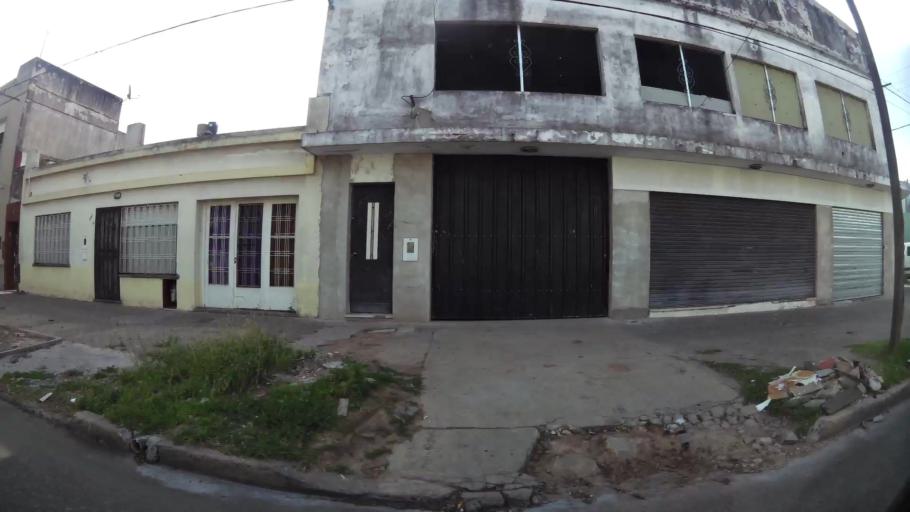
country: AR
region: Santa Fe
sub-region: Departamento de Rosario
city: Rosario
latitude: -32.9253
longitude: -60.6848
